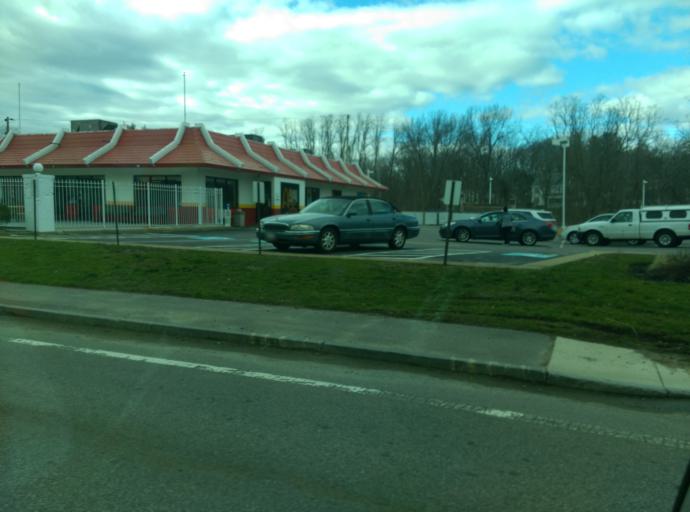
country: US
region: Massachusetts
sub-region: Essex County
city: Amesbury
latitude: 42.8465
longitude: -70.9130
